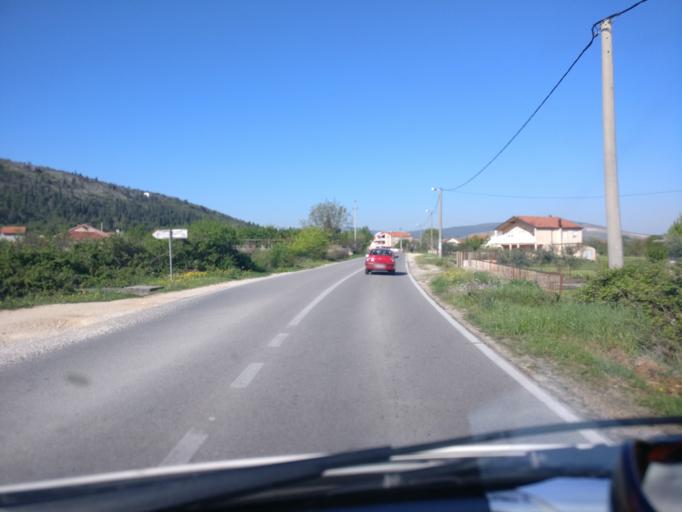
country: BA
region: Federation of Bosnia and Herzegovina
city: Tasovcici
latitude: 43.1202
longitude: 17.7435
